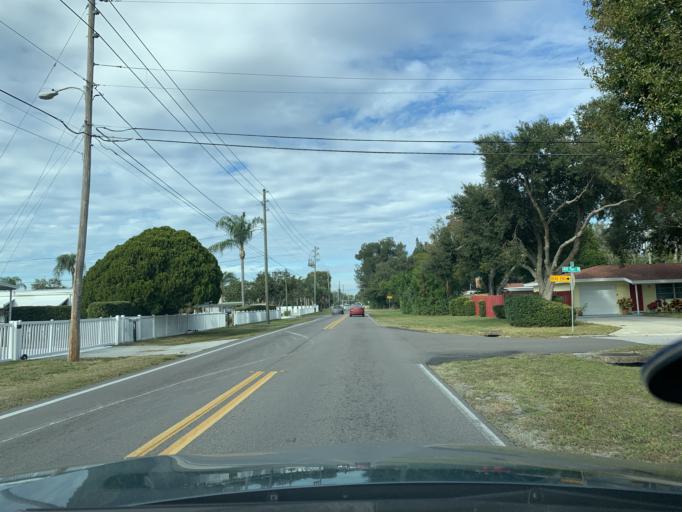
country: US
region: Florida
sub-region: Pinellas County
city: Kenneth City
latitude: 27.8087
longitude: -82.7369
